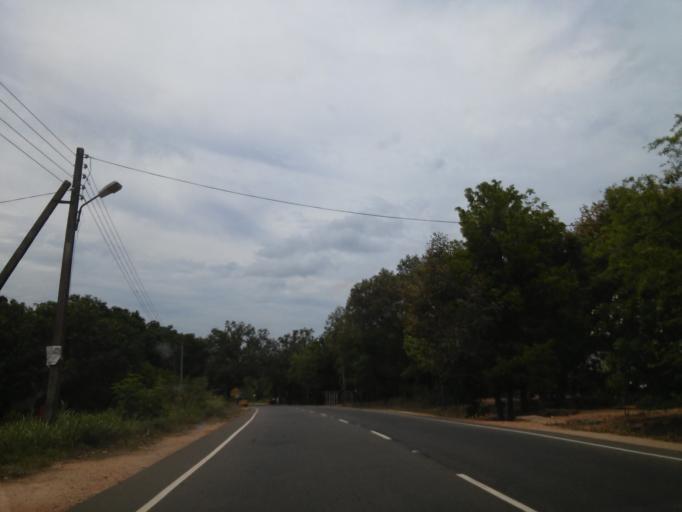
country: LK
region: Eastern Province
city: Trincomalee
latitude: 8.5630
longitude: 81.1565
